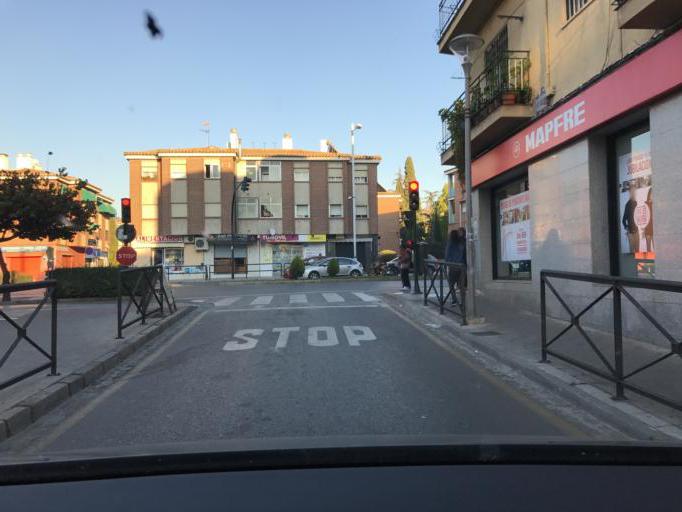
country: ES
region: Andalusia
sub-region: Provincia de Granada
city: Granada
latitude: 37.1951
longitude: -3.6095
